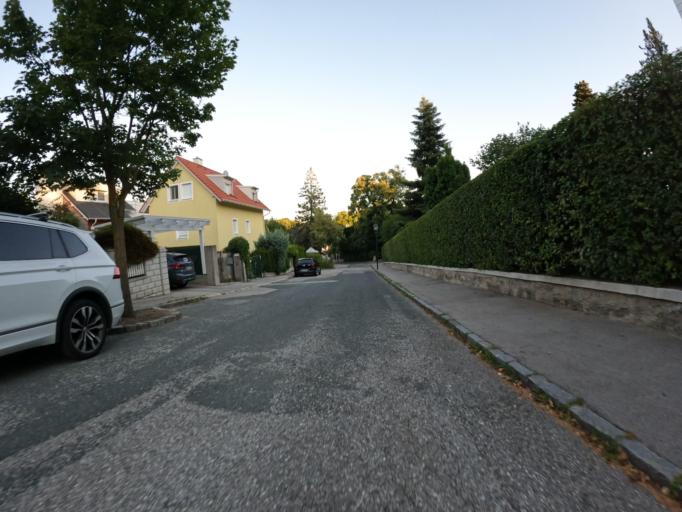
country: AT
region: Lower Austria
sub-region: Politischer Bezirk Baden
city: Baden
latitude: 48.0119
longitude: 16.2238
